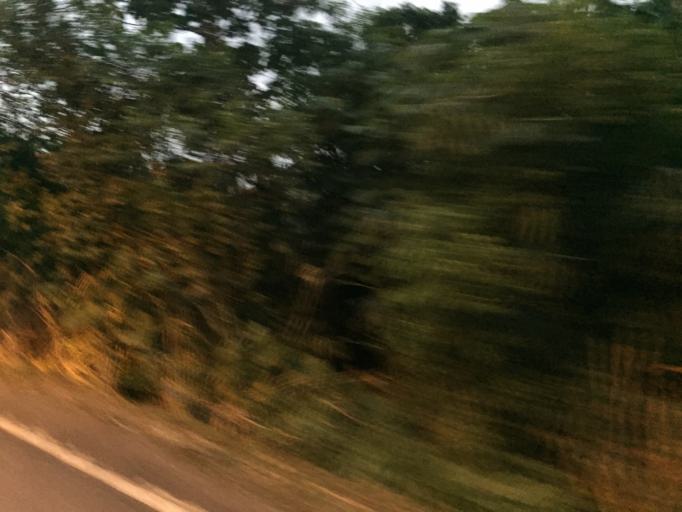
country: TW
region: Taiwan
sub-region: Yilan
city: Yilan
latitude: 24.7634
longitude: 121.7365
